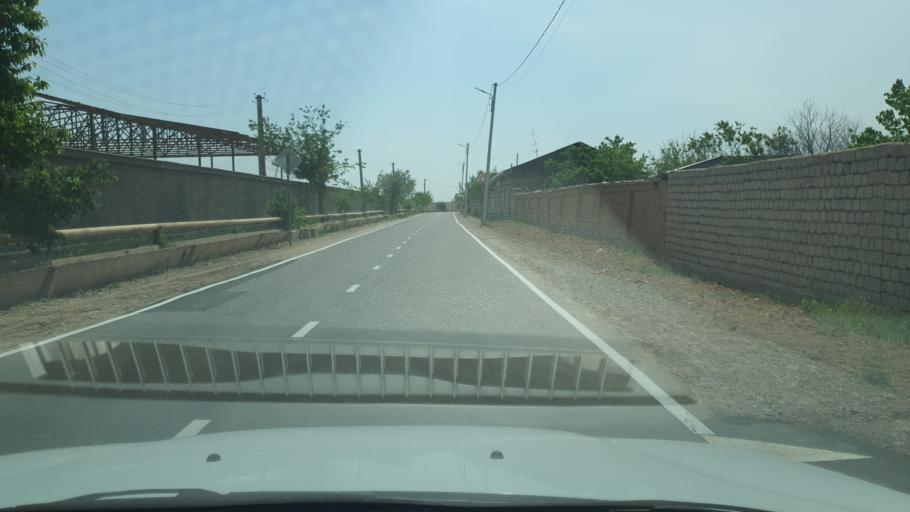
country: UZ
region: Toshkent
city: Salor
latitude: 41.4538
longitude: 69.4017
